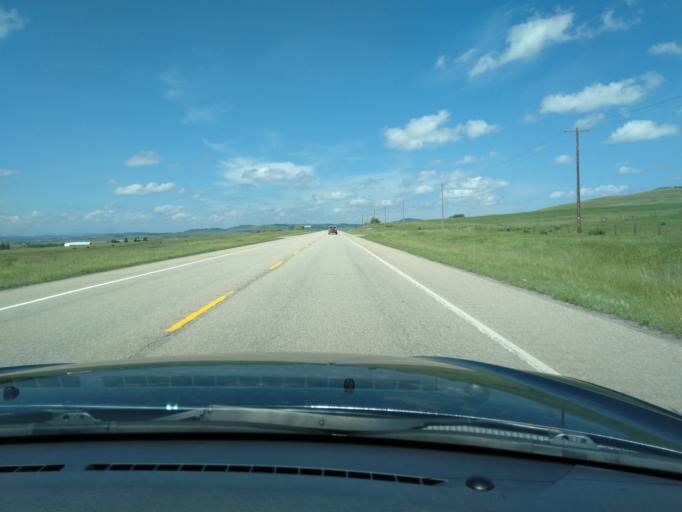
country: CA
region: Alberta
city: Cochrane
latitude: 51.2157
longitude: -114.5347
